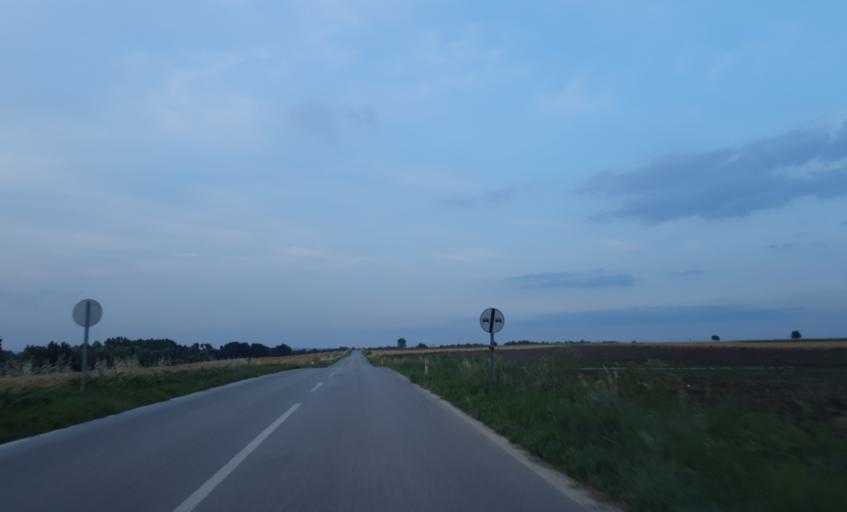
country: TR
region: Tekirdag
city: Beyazkoy
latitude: 41.3982
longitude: 27.6358
